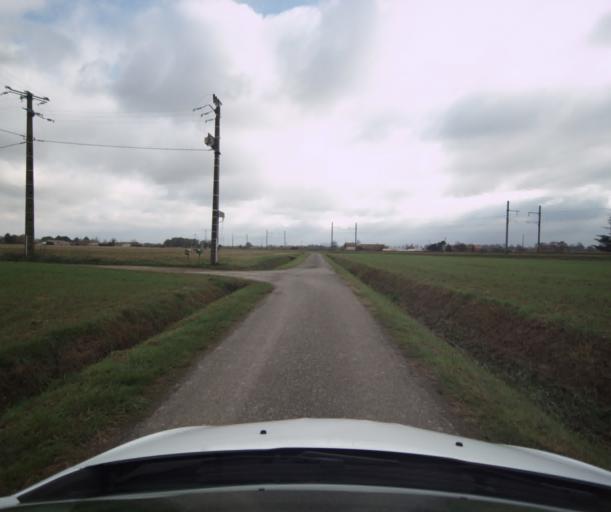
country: FR
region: Midi-Pyrenees
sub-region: Departement du Tarn-et-Garonne
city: Castelsarrasin
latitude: 44.0369
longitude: 1.1383
